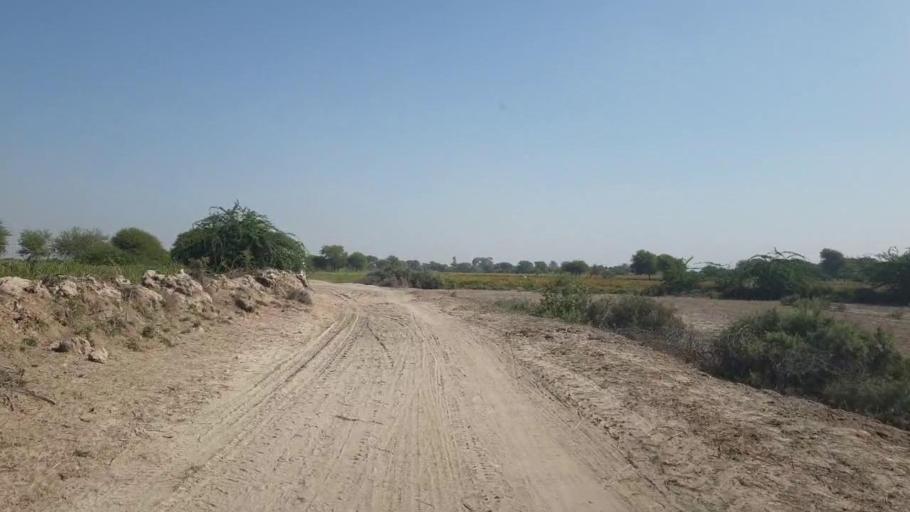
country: PK
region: Sindh
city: Talhar
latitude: 24.8257
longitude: 68.7885
